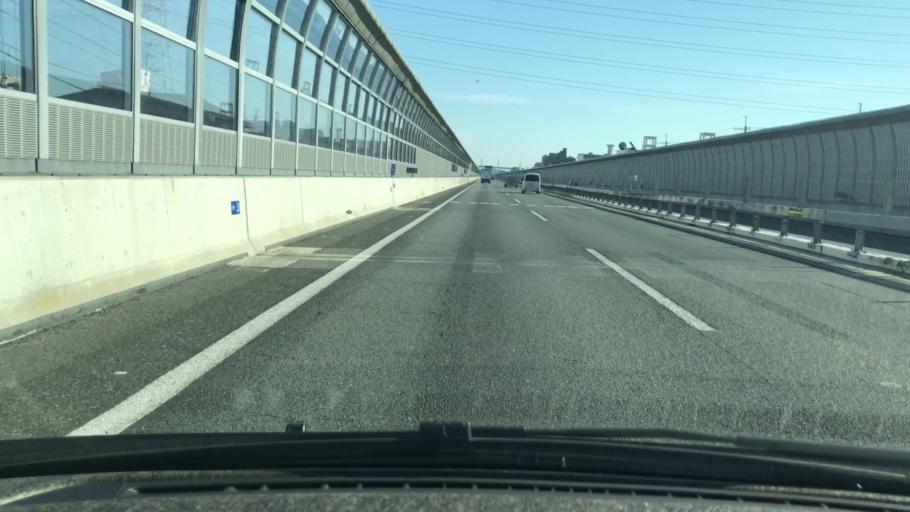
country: JP
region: Hyogo
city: Amagasaki
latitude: 34.7440
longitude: 135.3864
